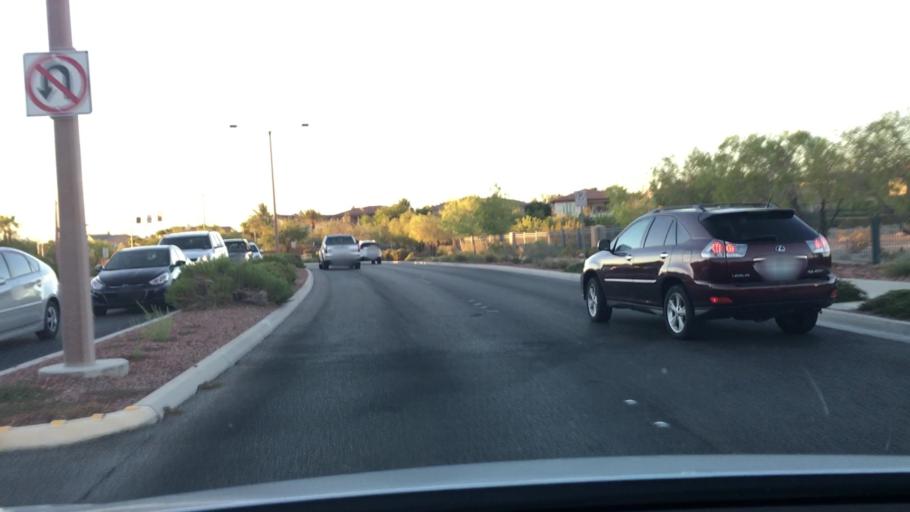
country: US
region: Nevada
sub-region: Clark County
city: Summerlin South
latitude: 36.1571
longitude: -115.3517
